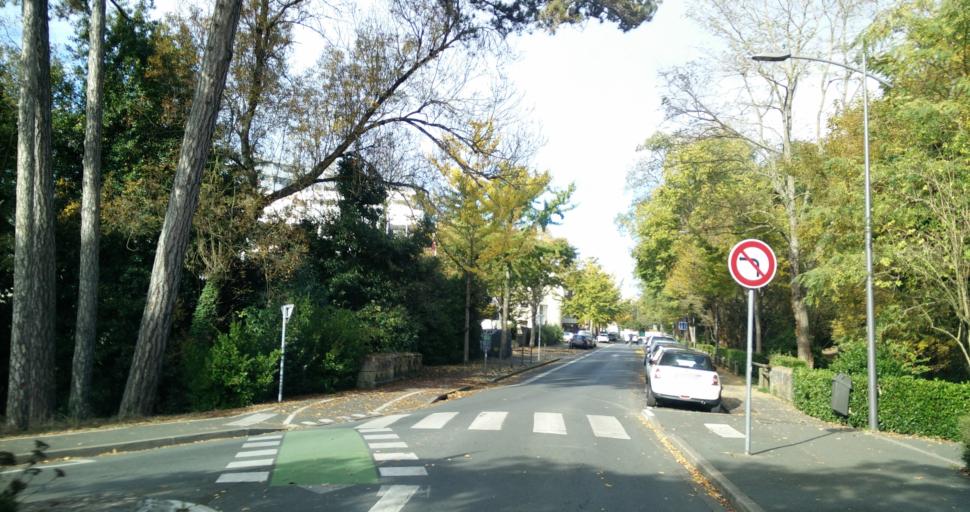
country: FR
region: Poitou-Charentes
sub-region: Departement de la Charente-Maritime
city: La Rochelle
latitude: 46.1606
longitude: -1.1578
